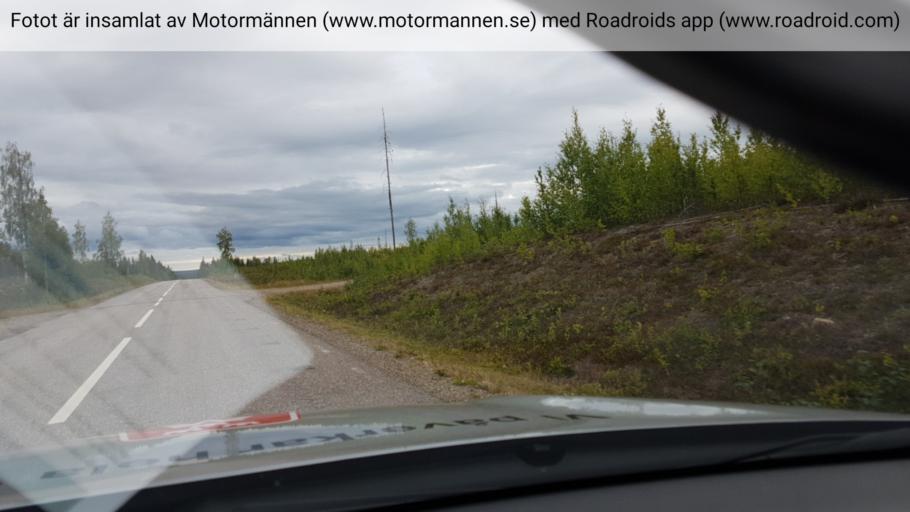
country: SE
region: Norrbotten
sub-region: Overkalix Kommun
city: OEverkalix
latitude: 66.8156
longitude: 23.0041
